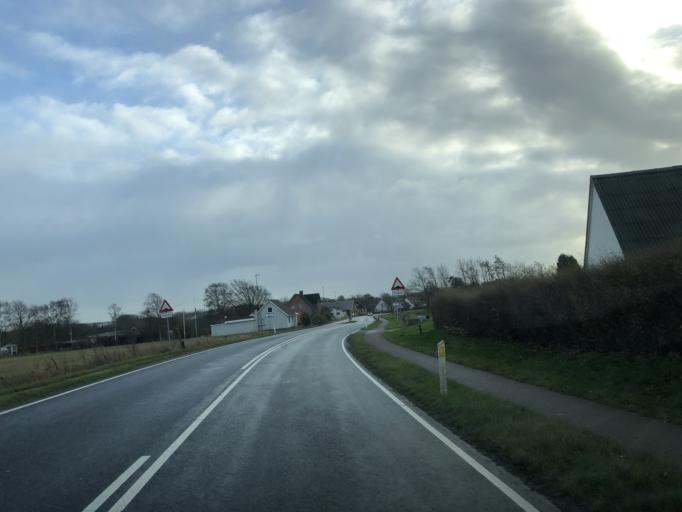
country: DK
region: North Denmark
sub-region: Rebild Kommune
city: Stovring
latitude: 56.8942
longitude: 9.7813
